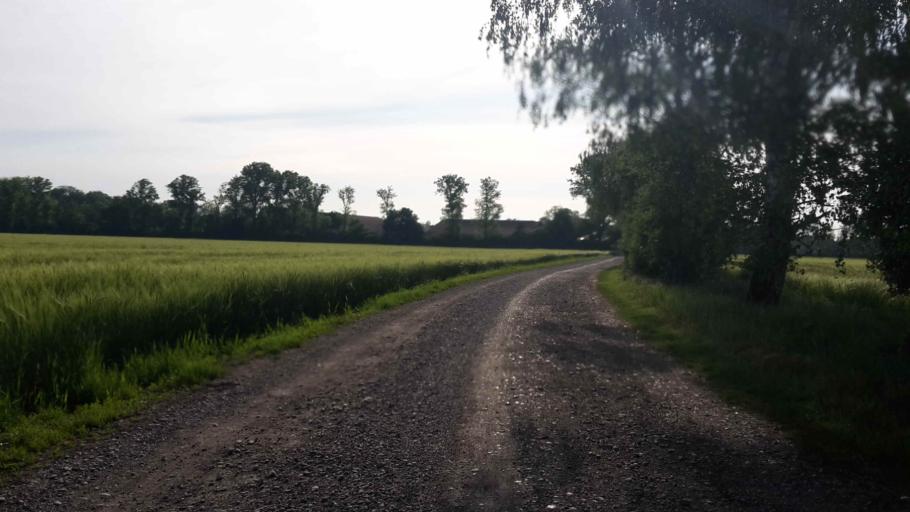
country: DE
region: Bavaria
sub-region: Upper Bavaria
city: Oberschleissheim
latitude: 48.2458
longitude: 11.5396
